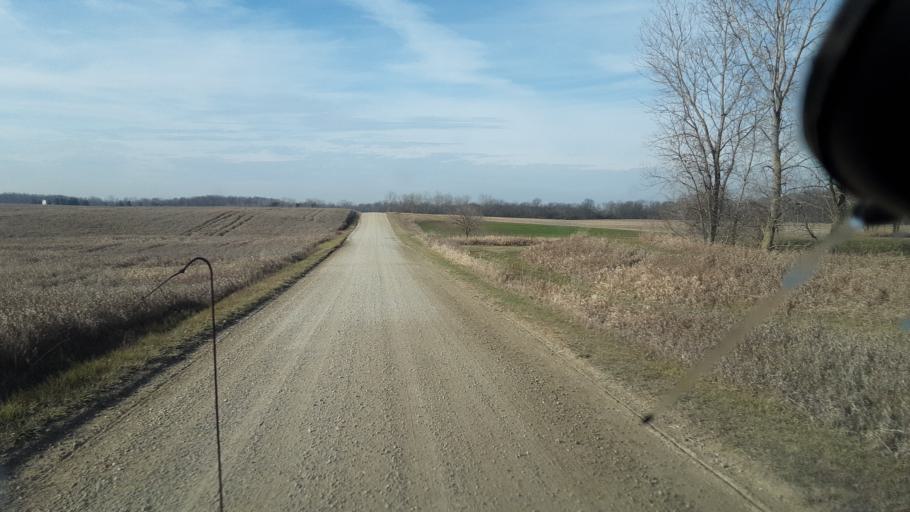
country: US
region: Ohio
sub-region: Defiance County
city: Hicksville
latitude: 41.2708
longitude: -84.8142
